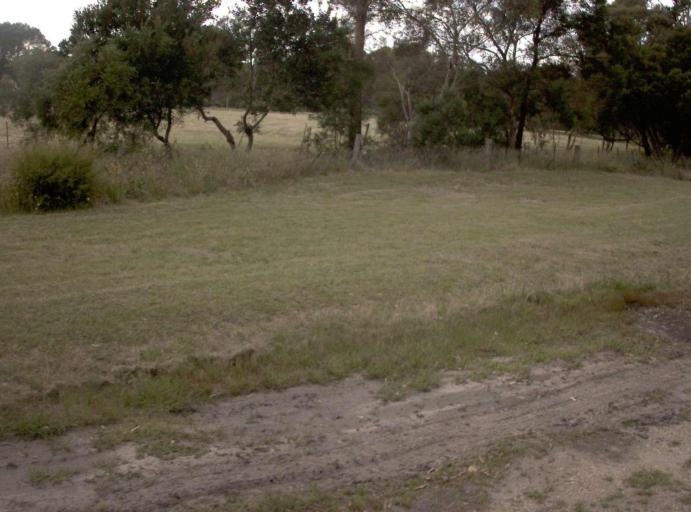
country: AU
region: Victoria
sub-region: Wellington
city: Sale
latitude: -38.0041
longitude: 147.2619
